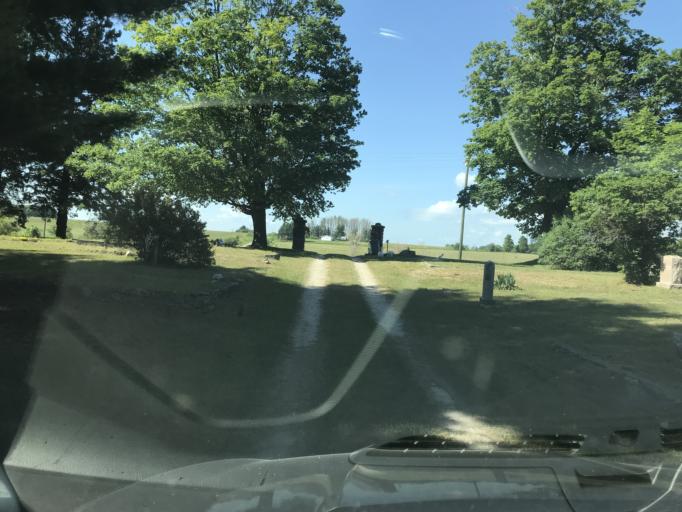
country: US
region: Michigan
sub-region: Cheboygan County
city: Cheboygan
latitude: 45.6212
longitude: -84.6501
